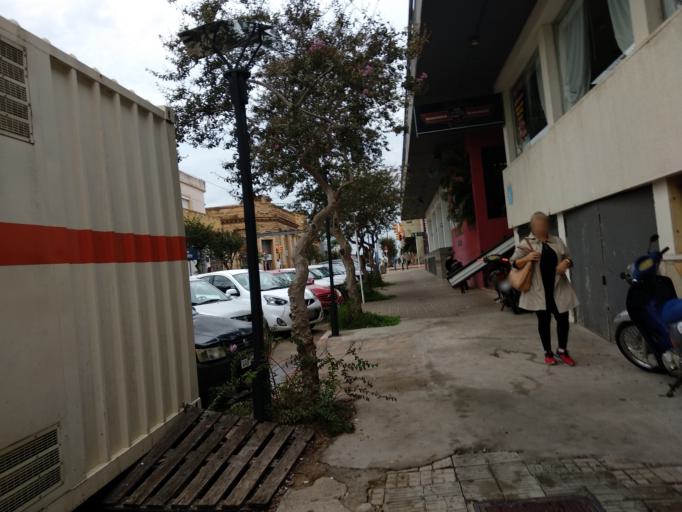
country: UY
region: Artigas
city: Artigas
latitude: -30.4021
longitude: -56.4677
